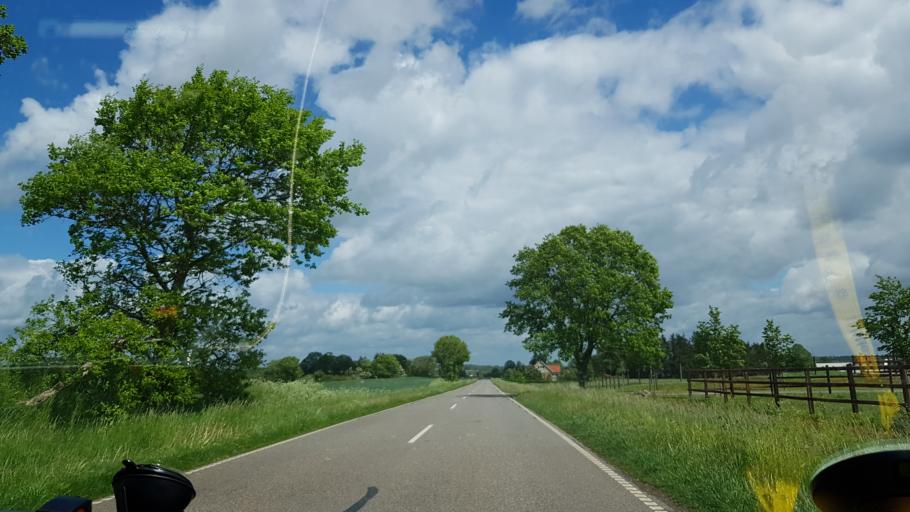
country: DK
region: South Denmark
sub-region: Kolding Kommune
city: Christiansfeld
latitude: 55.3384
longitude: 9.4603
